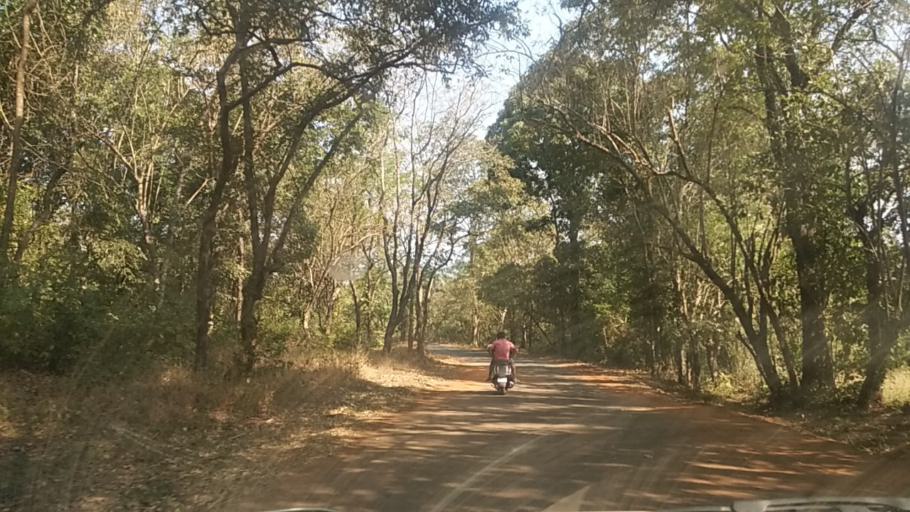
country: IN
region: Goa
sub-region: South Goa
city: Sanguem
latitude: 15.1912
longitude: 74.2280
